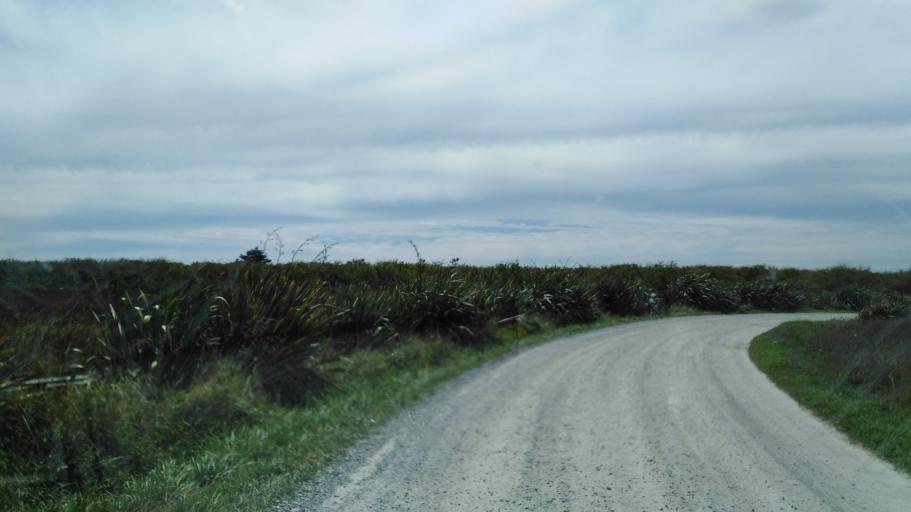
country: NZ
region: West Coast
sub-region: Buller District
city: Westport
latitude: -41.7369
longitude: 171.6042
